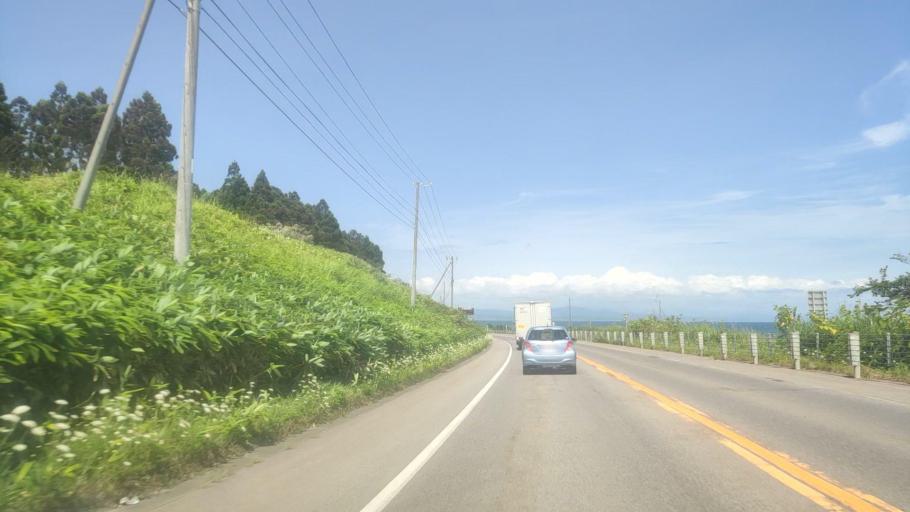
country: JP
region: Hokkaido
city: Nanae
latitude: 42.2056
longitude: 140.4051
